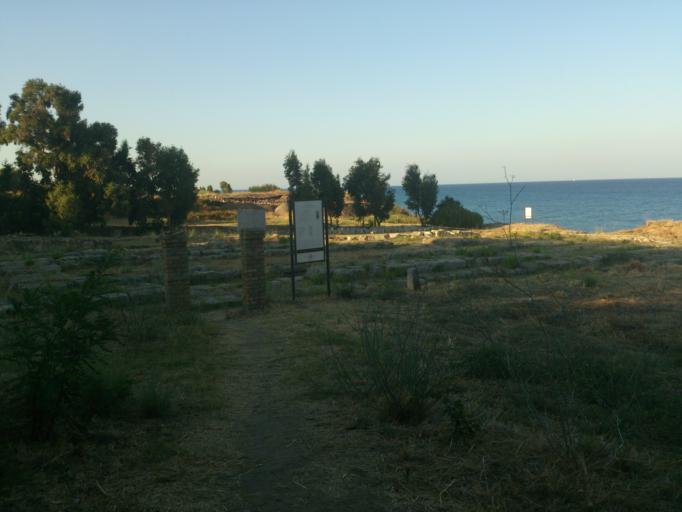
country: IT
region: Calabria
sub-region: Provincia di Reggio Calabria
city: Monasterace Marina
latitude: 38.4452
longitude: 16.5784
